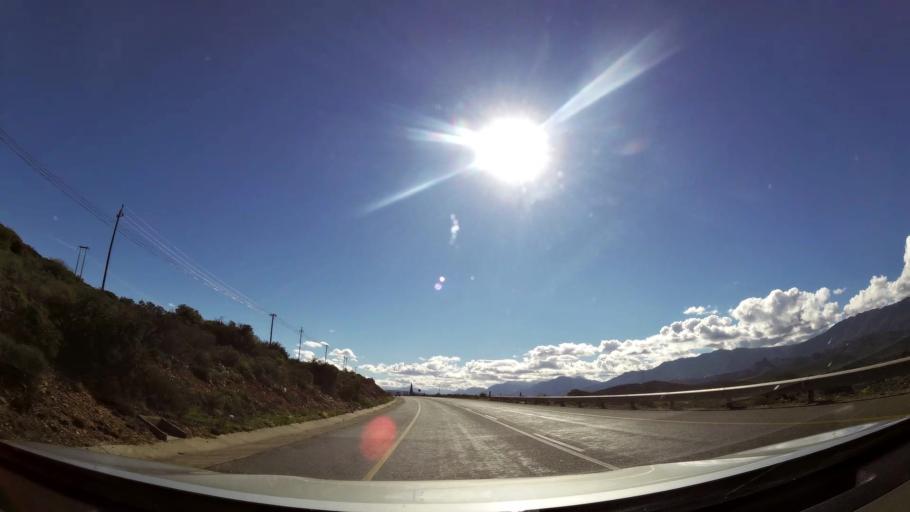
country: ZA
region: Western Cape
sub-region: Cape Winelands District Municipality
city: Ashton
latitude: -33.7793
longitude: 19.7652
